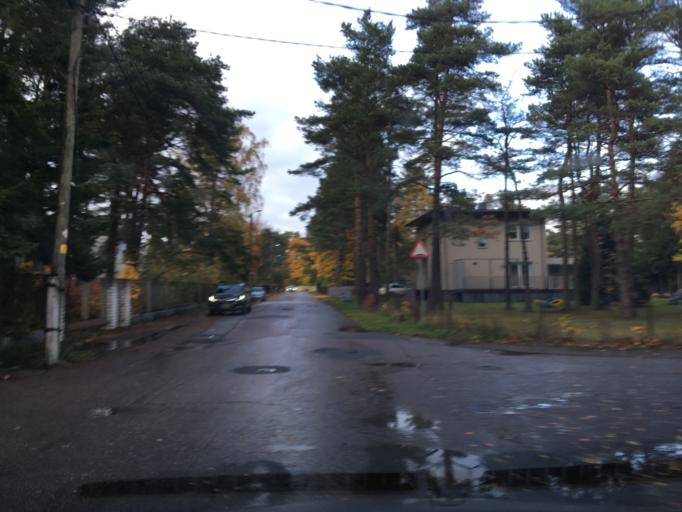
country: EE
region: Harju
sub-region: Tallinna linn
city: Tallinn
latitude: 59.3846
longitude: 24.7147
